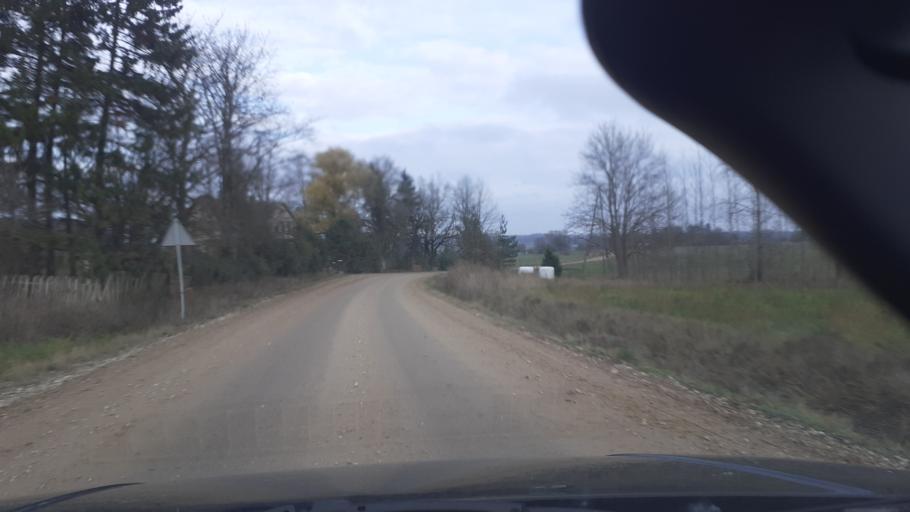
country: LV
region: Alsunga
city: Alsunga
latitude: 56.8638
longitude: 21.6731
